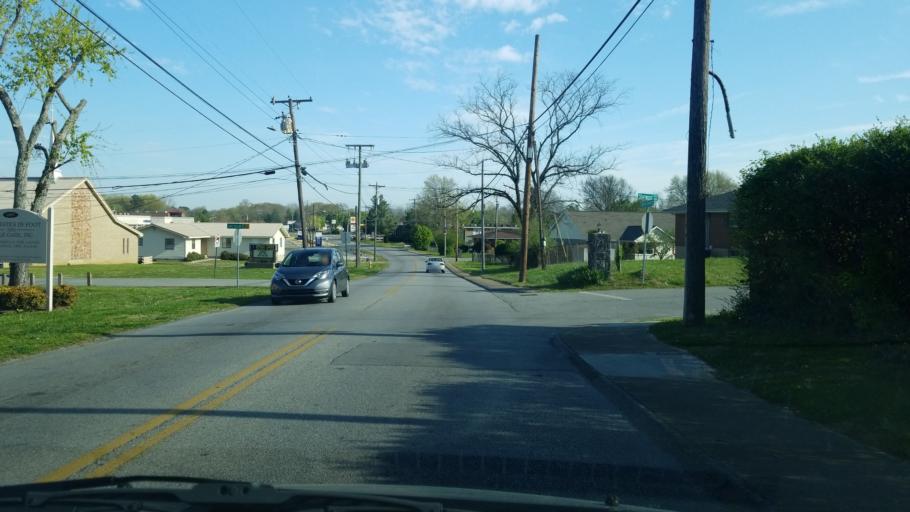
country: US
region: Tennessee
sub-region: Hamilton County
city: East Ridge
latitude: 34.9962
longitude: -85.2178
